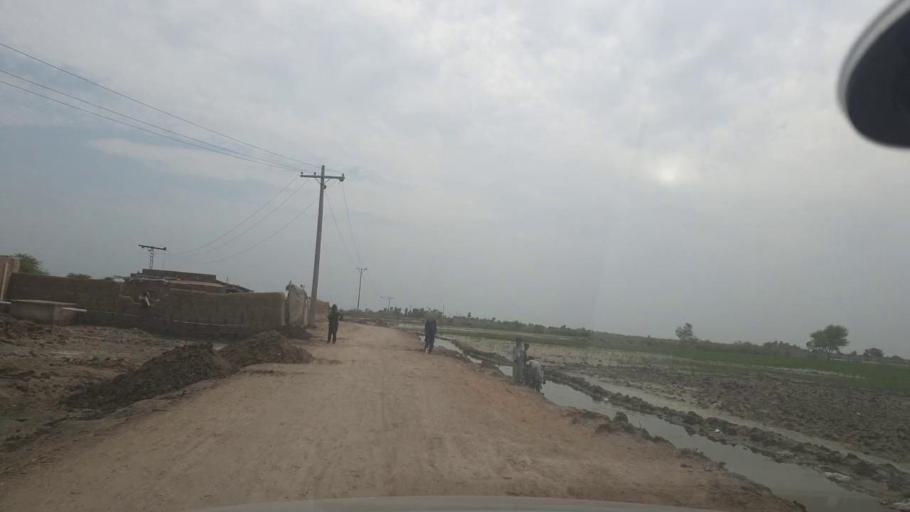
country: PK
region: Balochistan
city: Mehrabpur
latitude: 28.0506
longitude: 68.1365
